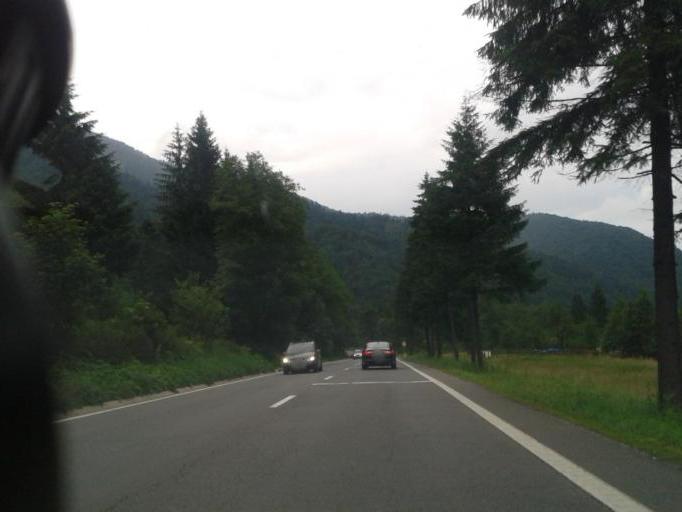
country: RO
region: Brasov
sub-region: Oras Predeal
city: Predeal
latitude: 45.5470
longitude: 25.5889
